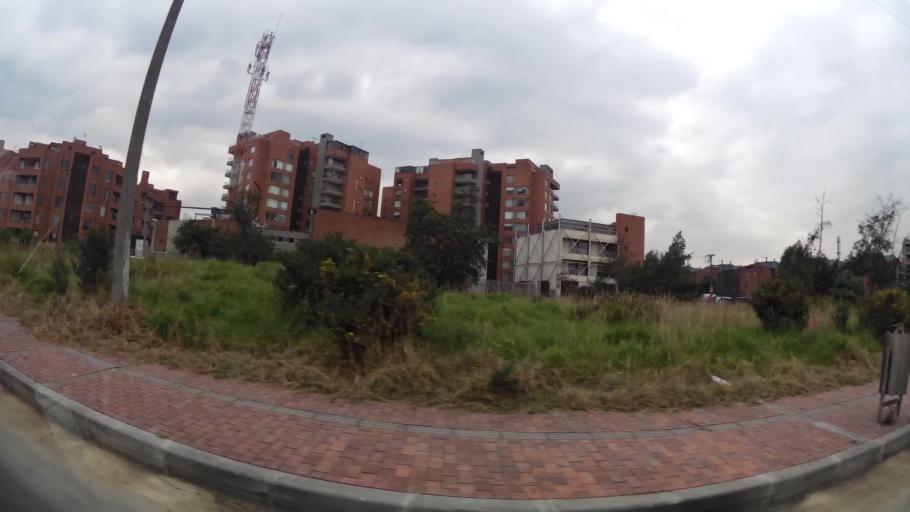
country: CO
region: Bogota D.C.
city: Bogota
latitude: 4.6641
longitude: -74.1126
